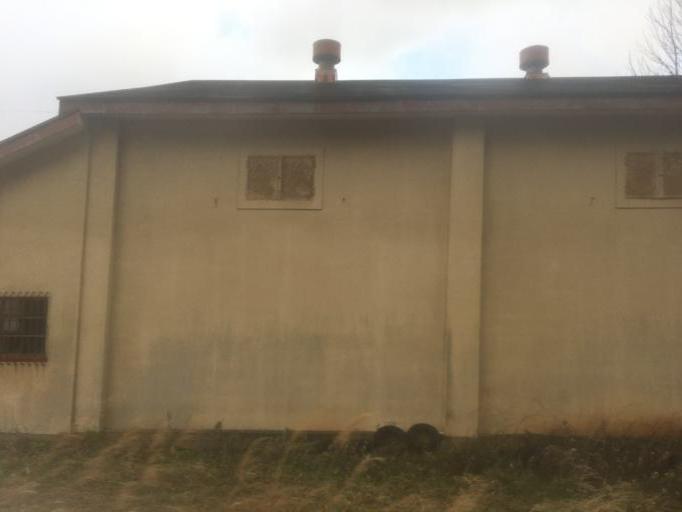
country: JP
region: Aomori
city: Goshogawara
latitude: 41.1825
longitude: 140.4860
